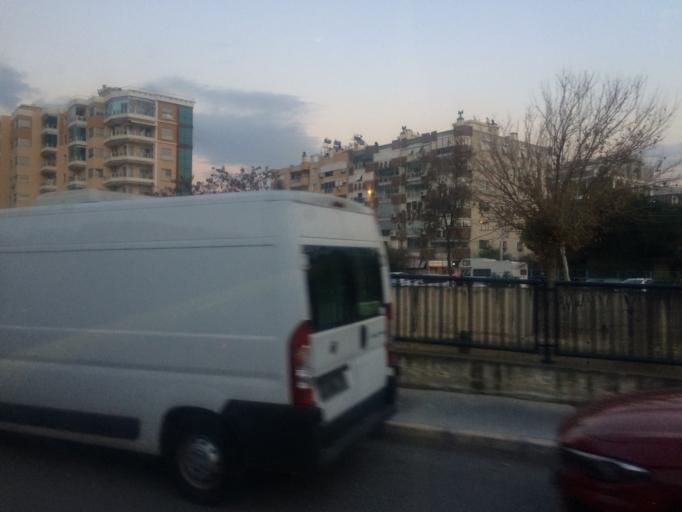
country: TR
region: Izmir
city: Karsiyaka
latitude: 38.4617
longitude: 27.0962
